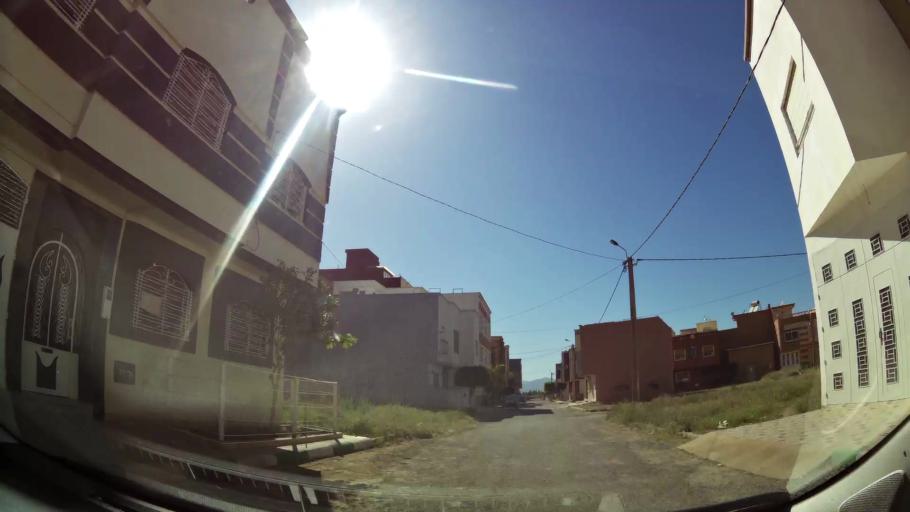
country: MA
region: Oriental
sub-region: Berkane-Taourirt
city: Berkane
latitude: 34.9407
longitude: -2.3410
